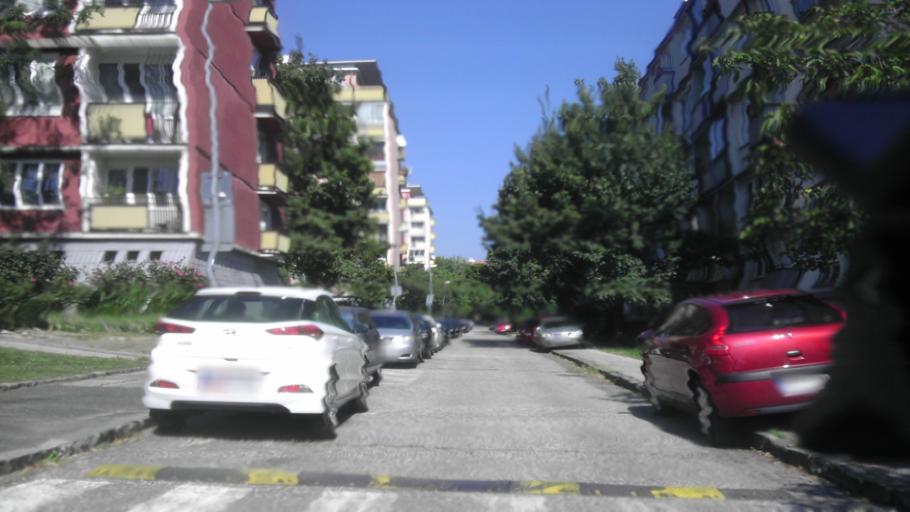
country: SK
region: Bratislavsky
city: Bratislava
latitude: 48.1606
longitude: 17.1188
